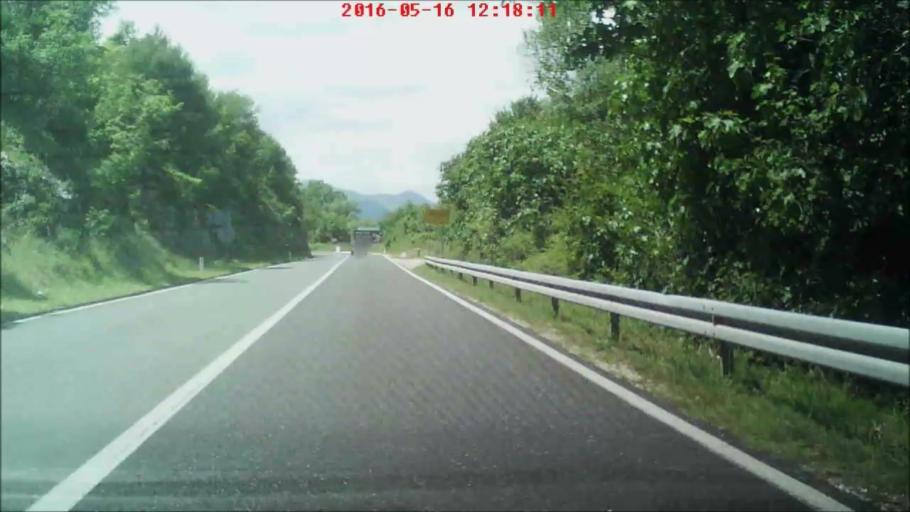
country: HR
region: Dubrovacko-Neretvanska
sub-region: Grad Dubrovnik
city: Metkovic
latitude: 43.0529
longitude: 17.6822
